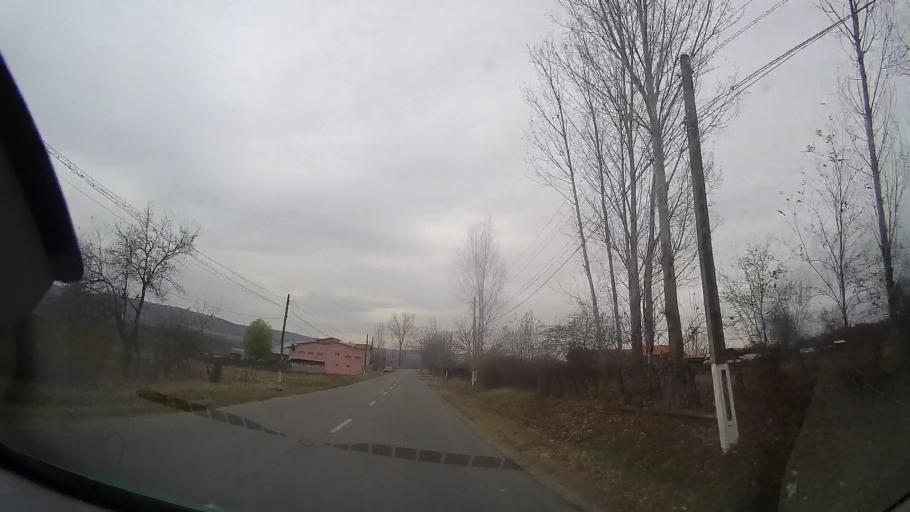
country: RO
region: Prahova
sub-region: Comuna Iordachianu
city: Iordacheanu
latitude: 45.0357
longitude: 26.2393
